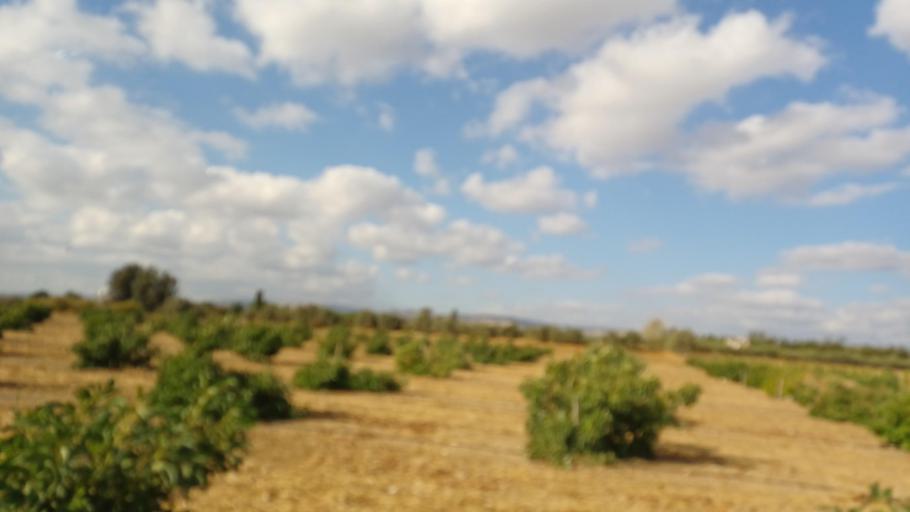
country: CY
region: Limassol
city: Pissouri
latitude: 34.7023
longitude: 32.5568
